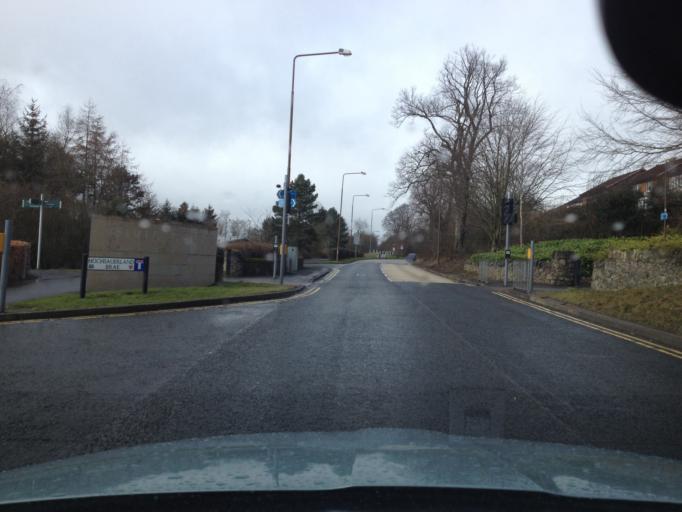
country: GB
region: Scotland
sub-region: West Lothian
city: Livingston
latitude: 55.8880
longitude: -3.5168
